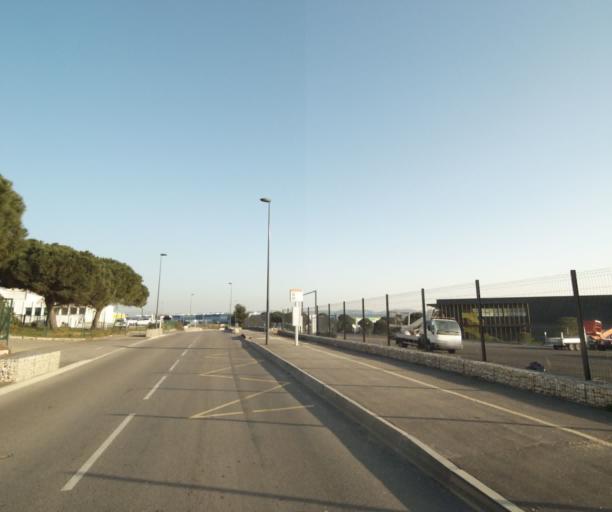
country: FR
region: Provence-Alpes-Cote d'Azur
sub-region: Departement des Bouches-du-Rhone
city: Saint-Victoret
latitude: 43.4323
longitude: 5.2474
